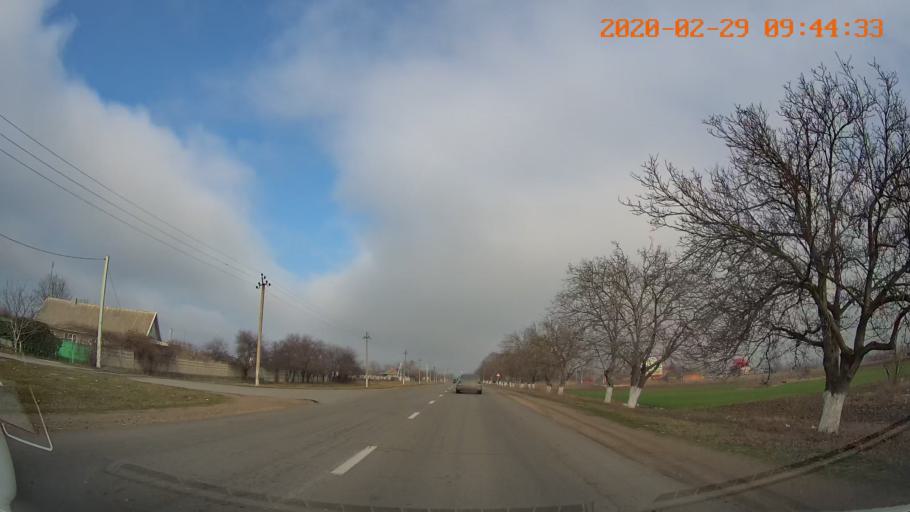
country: MD
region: Telenesti
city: Crasnoe
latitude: 46.6537
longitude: 29.8156
